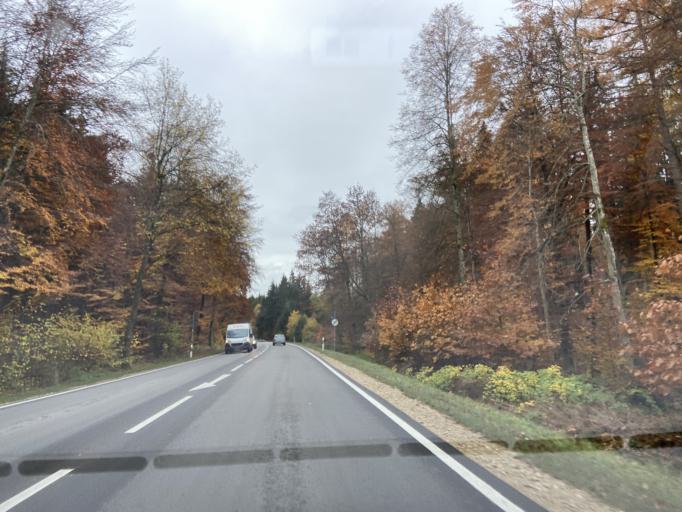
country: DE
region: Baden-Wuerttemberg
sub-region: Tuebingen Region
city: Krauchenwies
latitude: 48.0541
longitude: 9.2321
